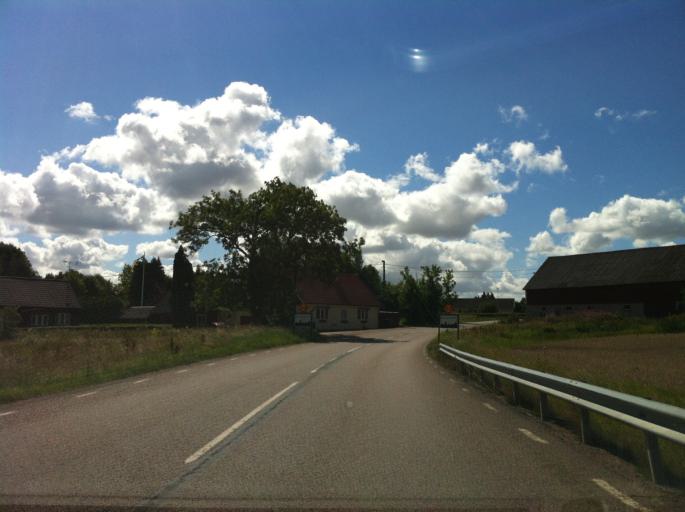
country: SE
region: Skane
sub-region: Svalovs Kommun
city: Kagerod
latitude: 56.0604
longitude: 13.0673
